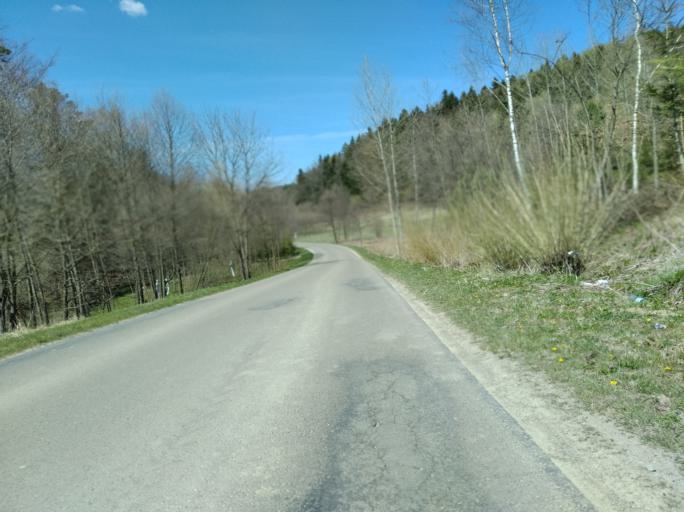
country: PL
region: Subcarpathian Voivodeship
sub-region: Powiat brzozowski
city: Golcowa
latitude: 49.7438
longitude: 22.0772
